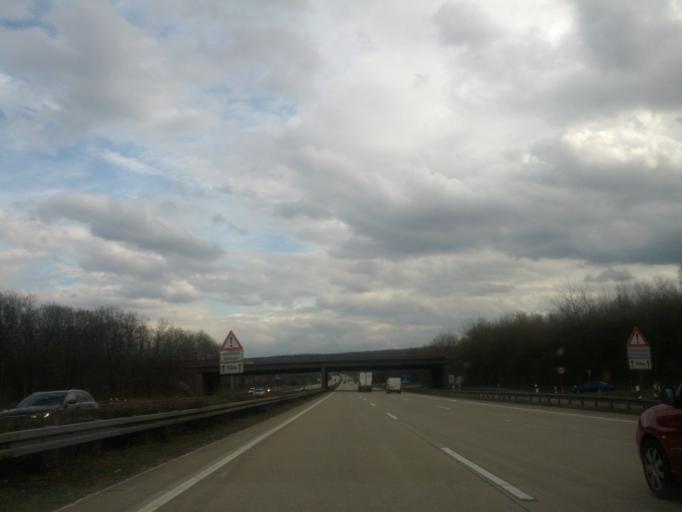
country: DE
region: Lower Saxony
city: Hildesheim
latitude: 52.1623
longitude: 9.9870
